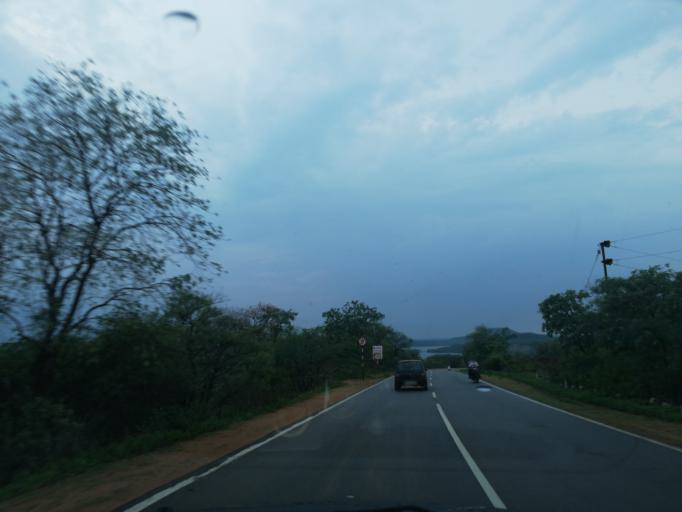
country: IN
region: Andhra Pradesh
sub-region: Guntur
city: Macherla
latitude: 16.6328
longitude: 79.2875
